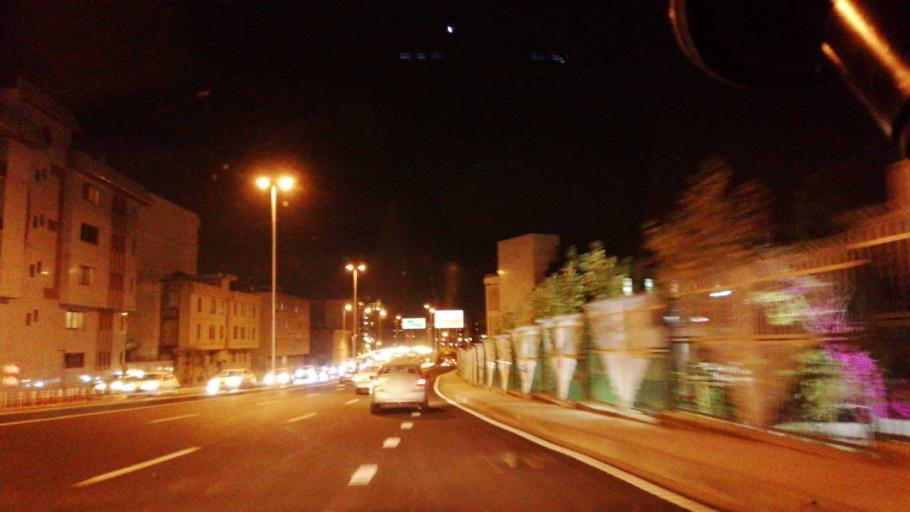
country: IR
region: Tehran
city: Tajrish
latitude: 35.7936
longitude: 51.4885
